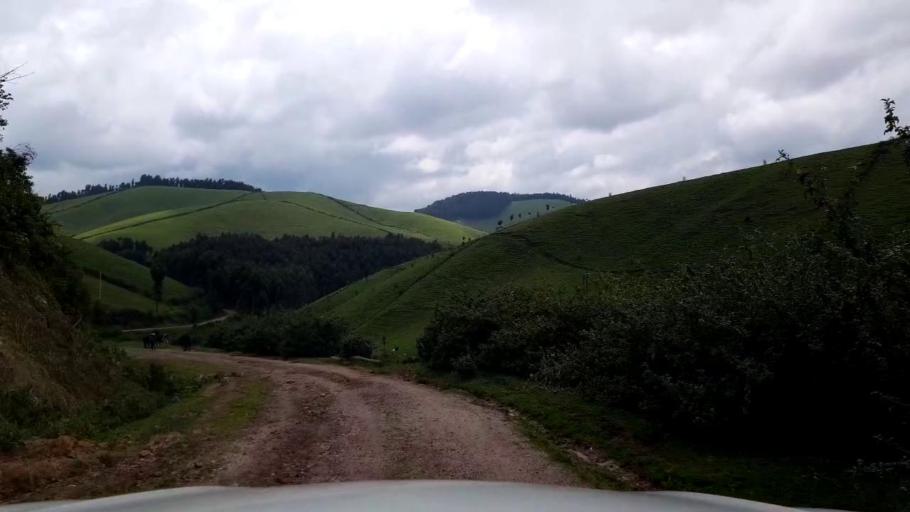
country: RW
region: Western Province
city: Gisenyi
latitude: -1.6816
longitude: 29.4171
